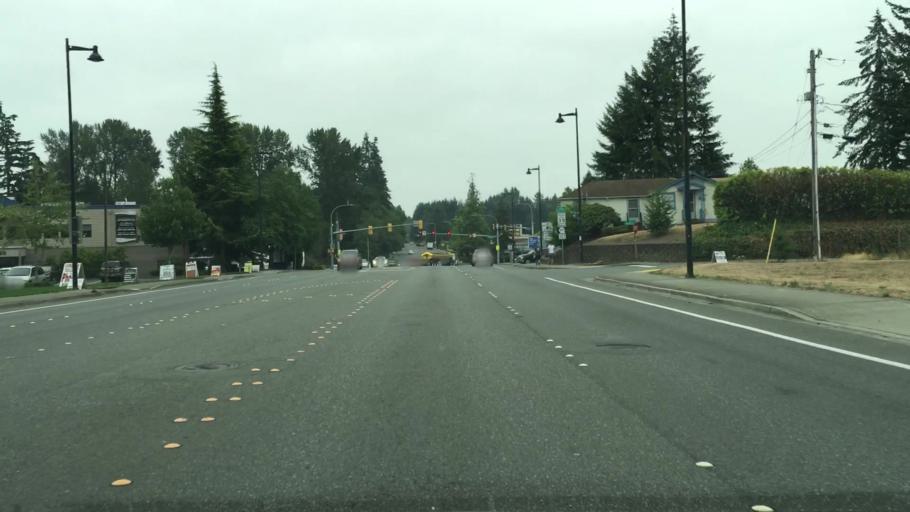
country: US
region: Washington
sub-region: King County
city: Newcastle
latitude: 47.5072
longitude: -122.1564
